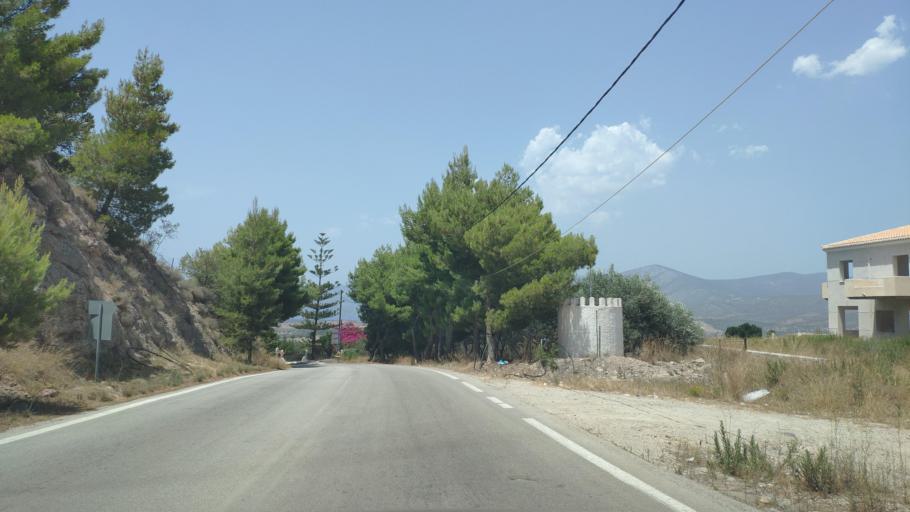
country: GR
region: Peloponnese
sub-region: Nomos Argolidos
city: Kranidi
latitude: 37.3761
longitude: 23.1493
